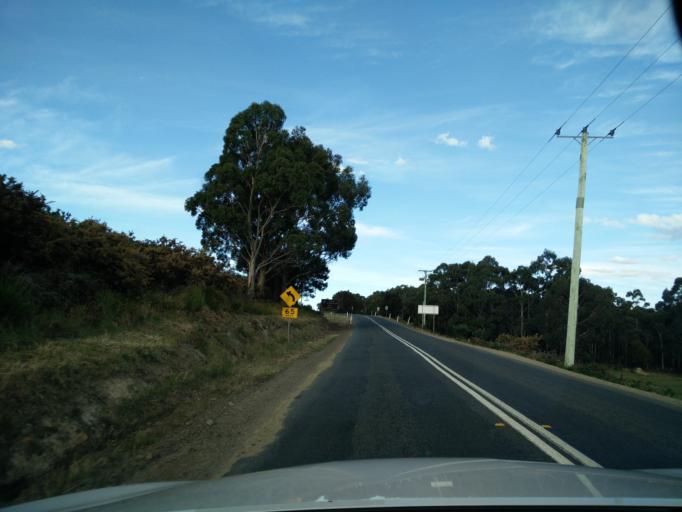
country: AU
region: Tasmania
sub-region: Break O'Day
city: St Helens
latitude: -41.9422
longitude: 148.2180
